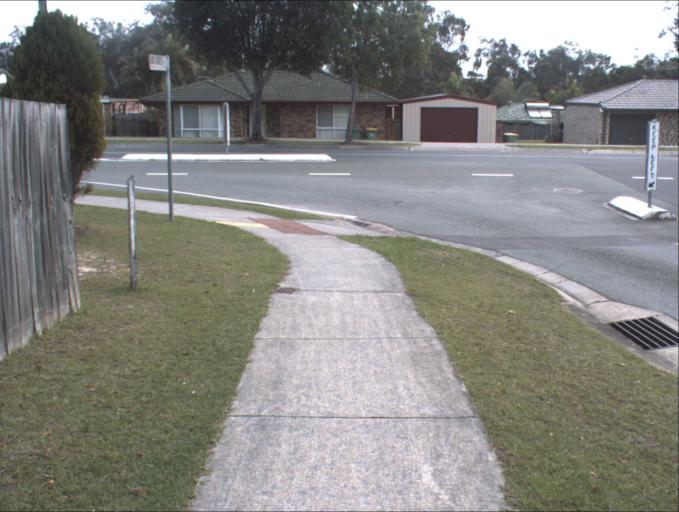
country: AU
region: Queensland
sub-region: Logan
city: Woodridge
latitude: -27.6723
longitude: 153.0819
